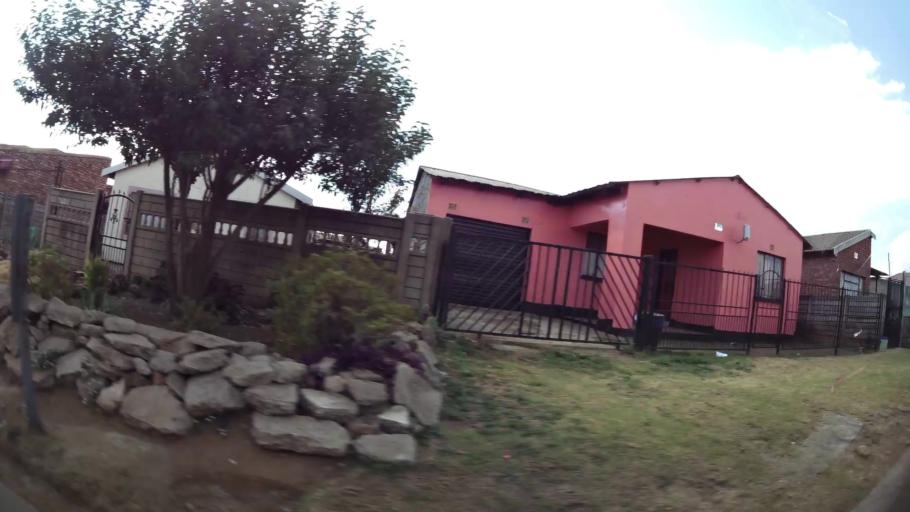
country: ZA
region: Gauteng
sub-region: Ekurhuleni Metropolitan Municipality
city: Springs
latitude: -26.1222
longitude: 28.4772
